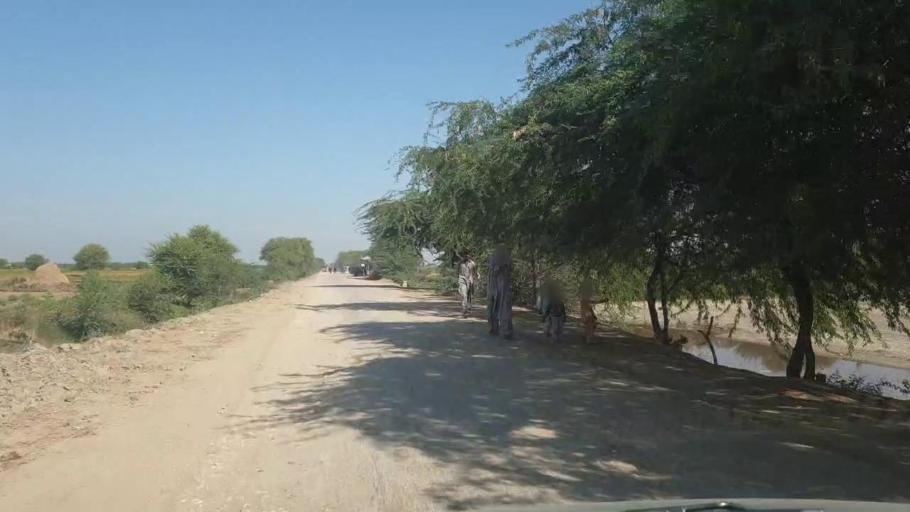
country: PK
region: Sindh
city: Tando Bago
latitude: 24.8003
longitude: 68.9772
